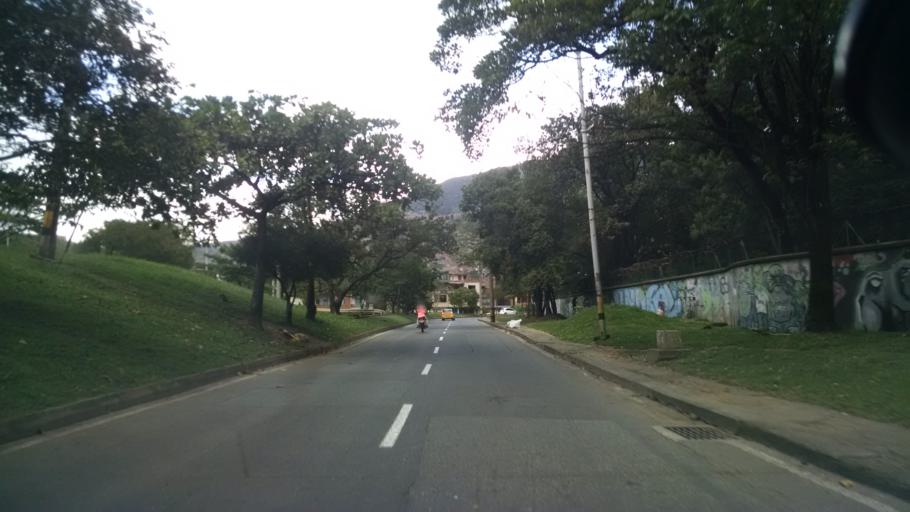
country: CO
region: Antioquia
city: Medellin
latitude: 6.2747
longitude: -75.5692
